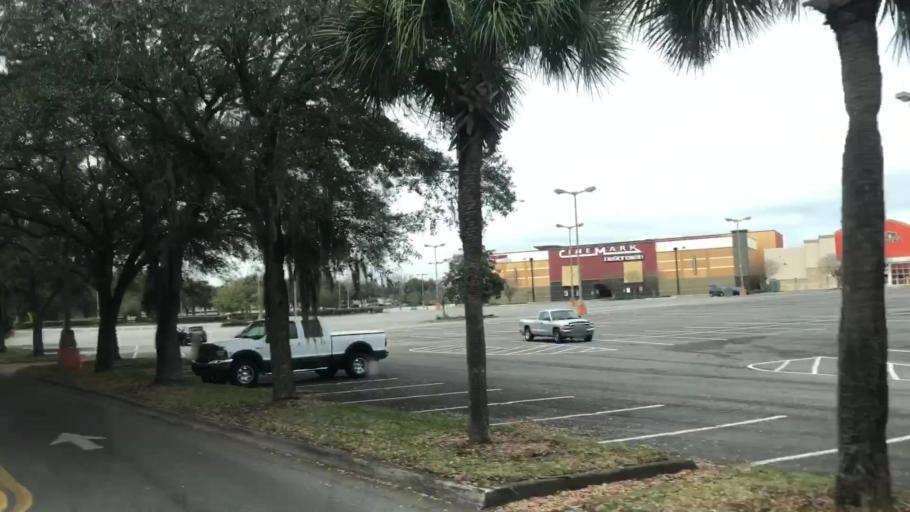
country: US
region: Florida
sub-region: Polk County
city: Gibsonia
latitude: 28.0894
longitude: -81.9759
